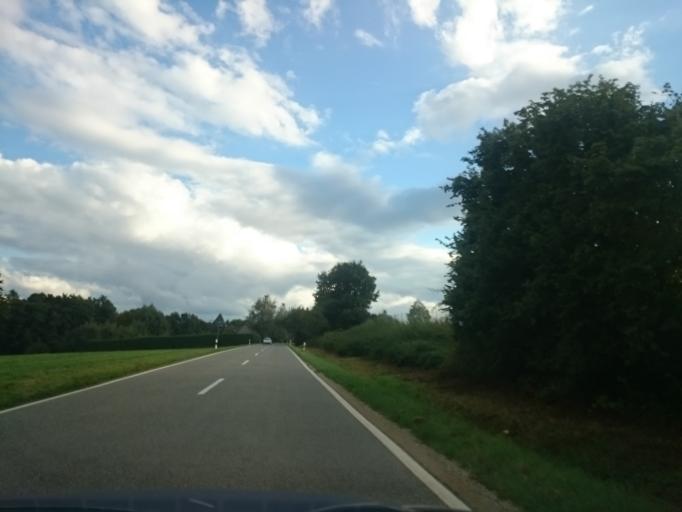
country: DE
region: Bavaria
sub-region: Regierungsbezirk Mittelfranken
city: Thalmassing
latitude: 49.1305
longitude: 11.1983
